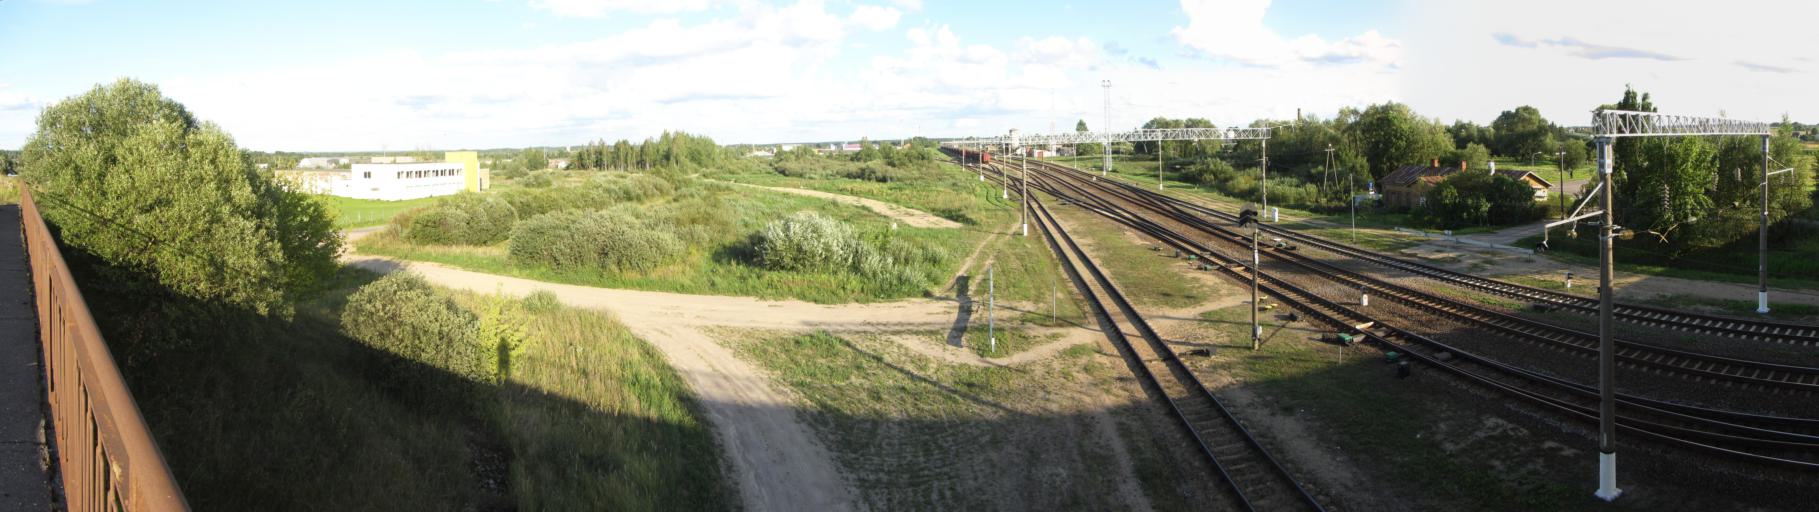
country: LT
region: Vilnius County
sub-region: Vilniaus Rajonas
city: Vievis
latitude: 54.7831
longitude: 24.8065
